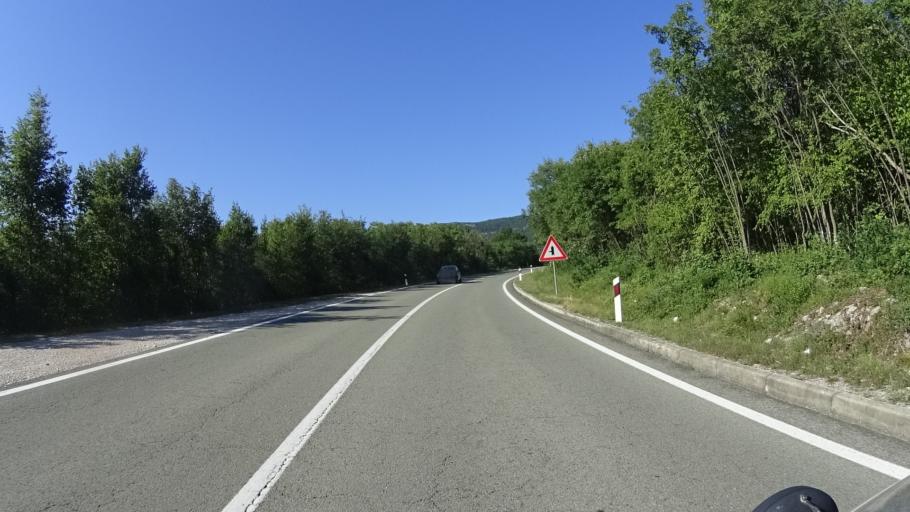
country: HR
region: Istarska
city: Lovran
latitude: 45.3119
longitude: 14.1342
